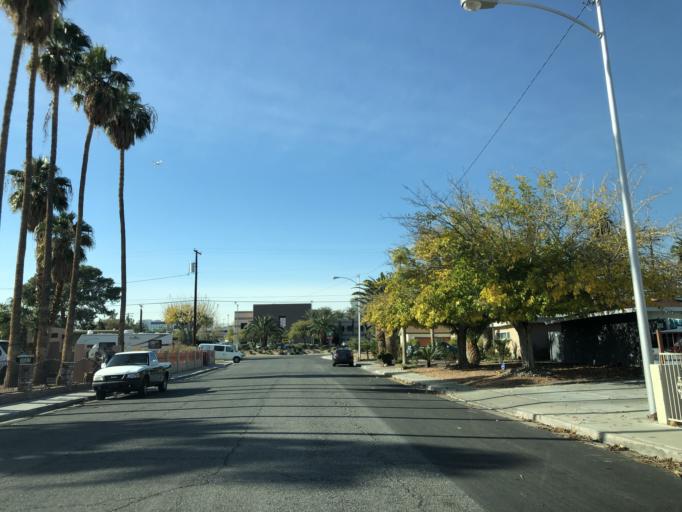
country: US
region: Nevada
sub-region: Clark County
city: Winchester
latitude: 36.1323
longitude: -115.1309
